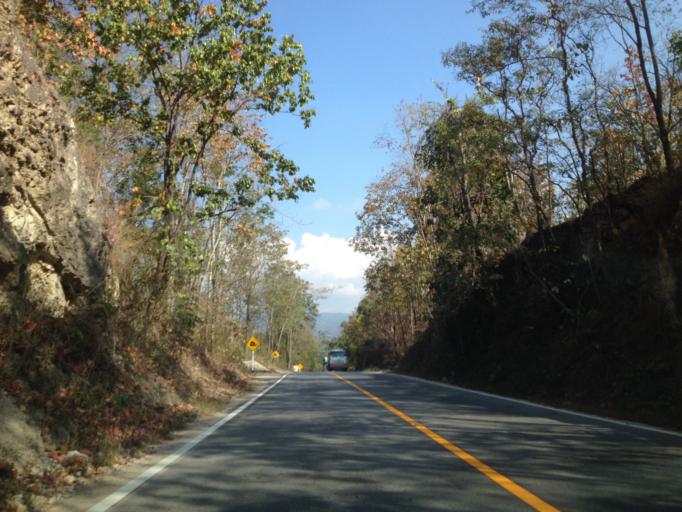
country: TH
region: Chiang Mai
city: Hot
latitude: 18.1772
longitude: 98.4516
